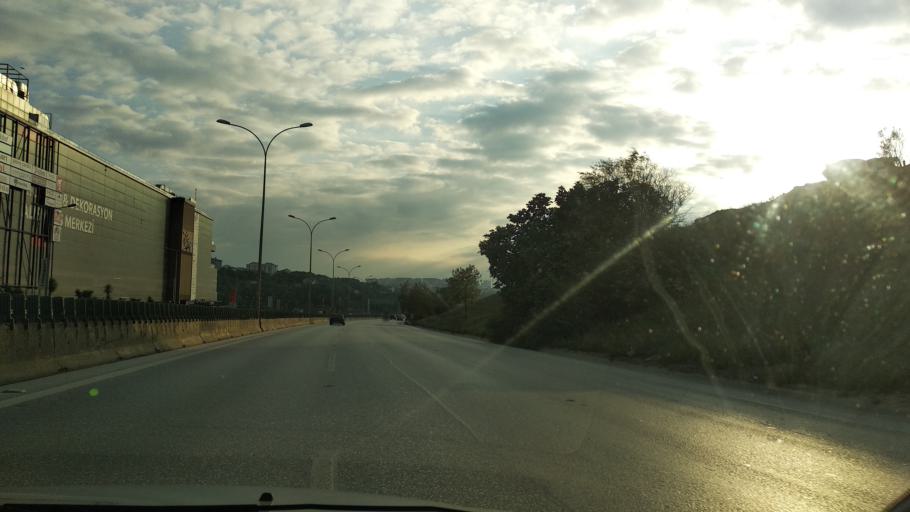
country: TR
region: Istanbul
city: Icmeler
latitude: 40.8881
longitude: 29.3244
